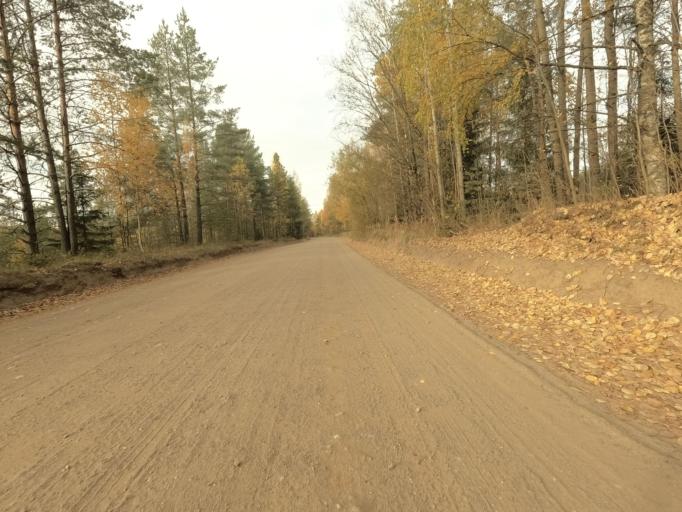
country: RU
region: Leningrad
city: Priladozhskiy
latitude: 59.6790
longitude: 31.3646
